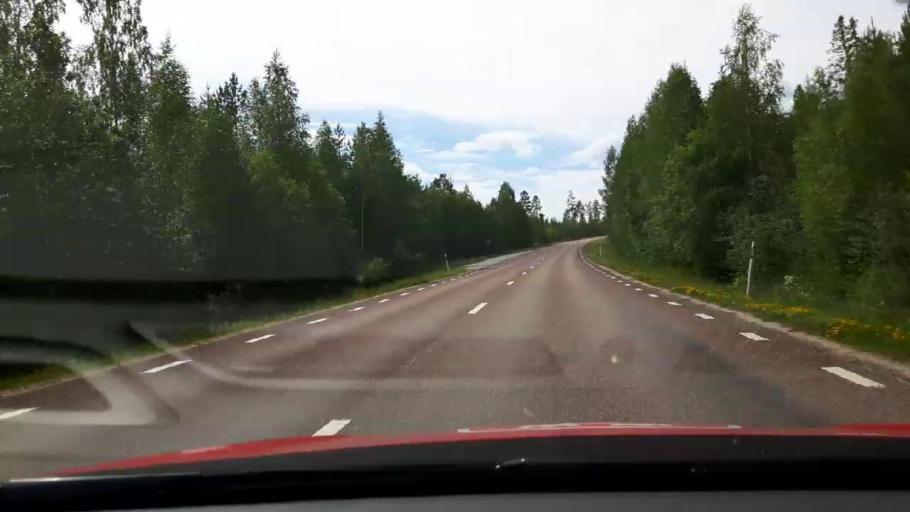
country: SE
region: Jaemtland
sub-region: Harjedalens Kommun
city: Sveg
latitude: 62.0517
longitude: 14.8973
